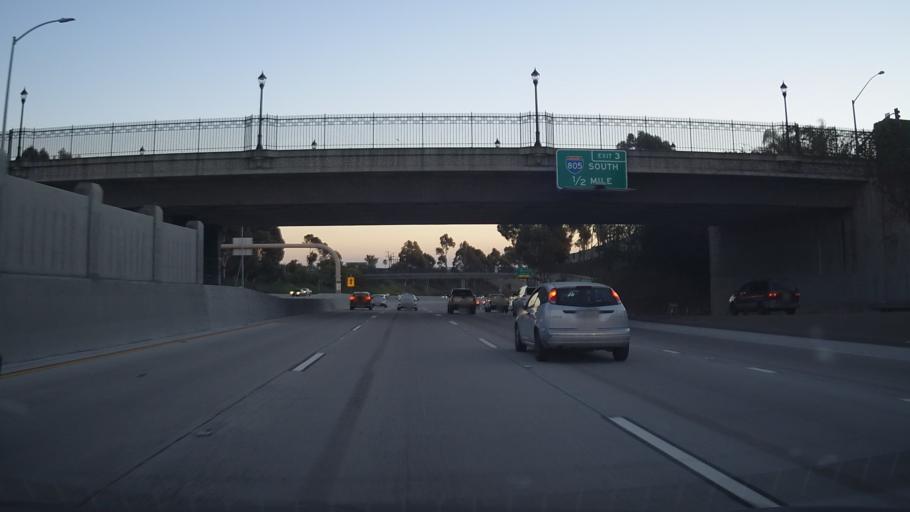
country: US
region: California
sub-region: San Diego County
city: San Diego
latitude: 32.7483
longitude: -117.1090
